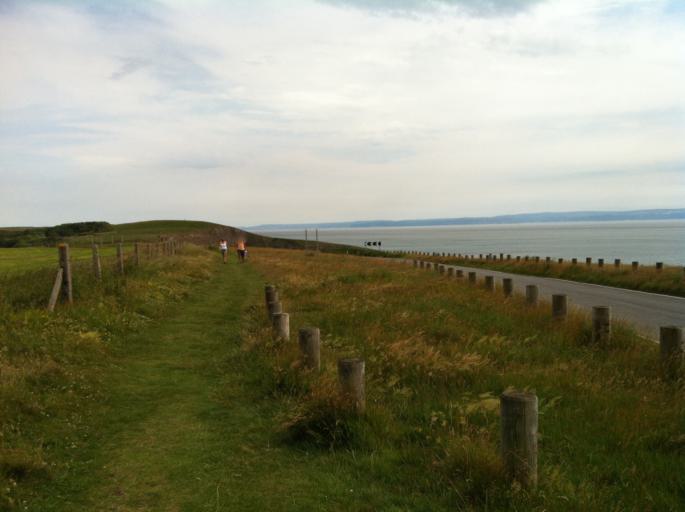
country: GB
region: Wales
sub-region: Bridgend county borough
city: Merthyr Mawr
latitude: 51.4487
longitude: -3.6097
